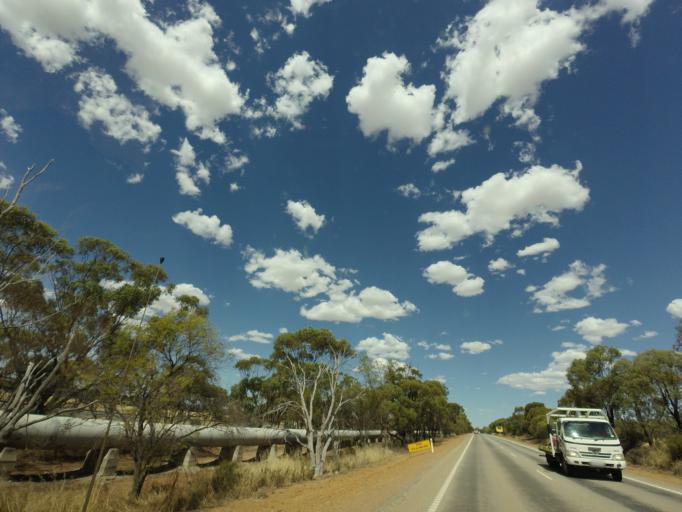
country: AU
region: Western Australia
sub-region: Cunderdin
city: Cunderdin
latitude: -31.6401
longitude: 117.1808
